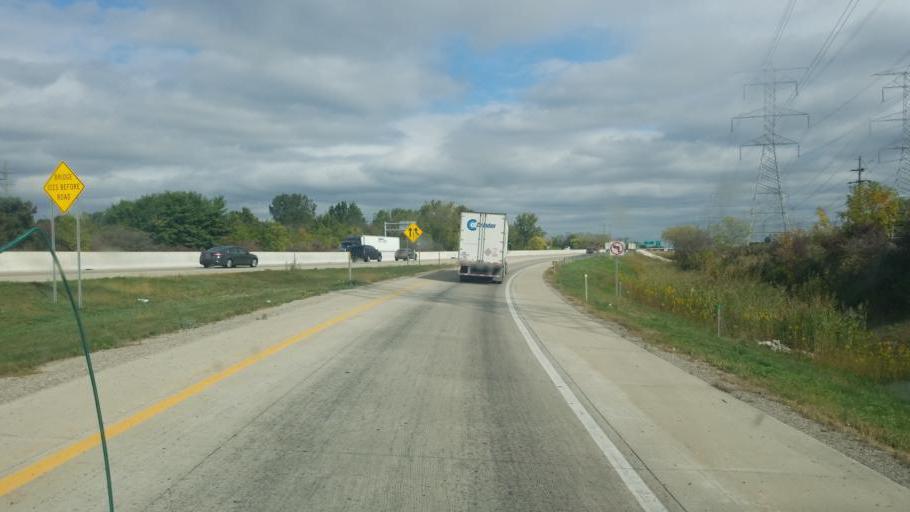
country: US
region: Michigan
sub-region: Monroe County
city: Detroit Beach
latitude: 41.9663
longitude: -83.3482
